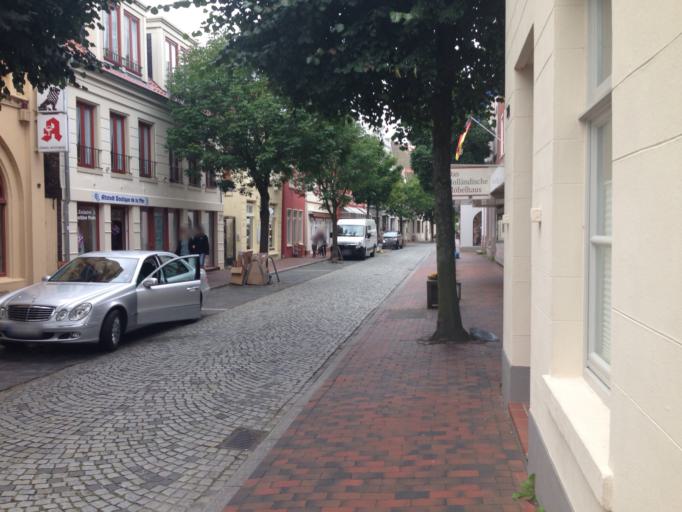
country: DE
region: Lower Saxony
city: Leer
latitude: 53.2285
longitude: 7.4509
